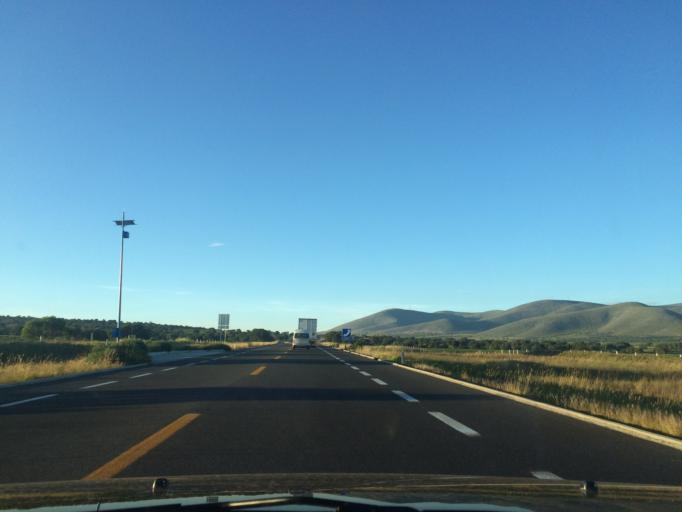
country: MX
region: Puebla
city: Cuacnopalan
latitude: 18.7711
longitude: -97.4851
